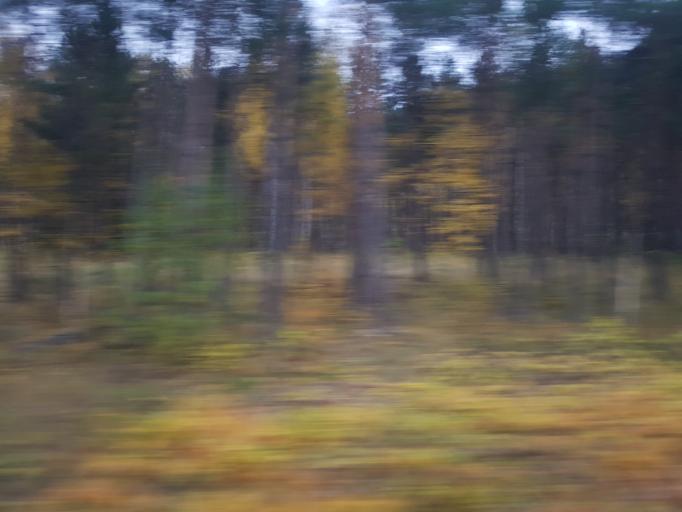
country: NO
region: Oppland
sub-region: Dovre
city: Dovre
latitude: 61.9157
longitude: 9.3484
